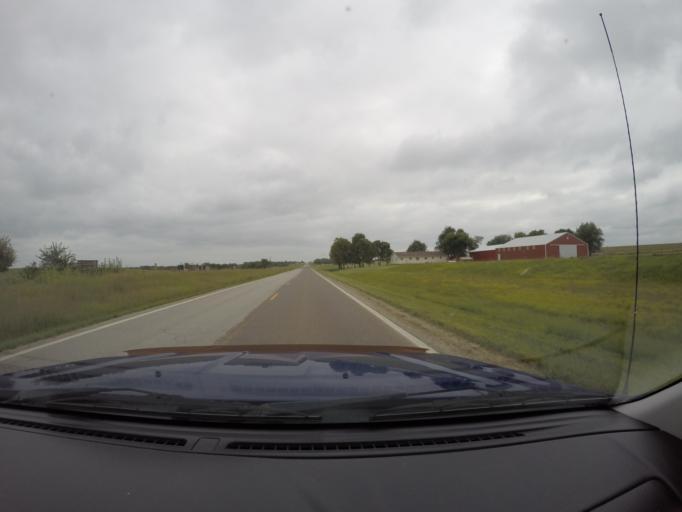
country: US
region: Kansas
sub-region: Morris County
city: Council Grove
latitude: 38.8516
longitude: -96.5015
